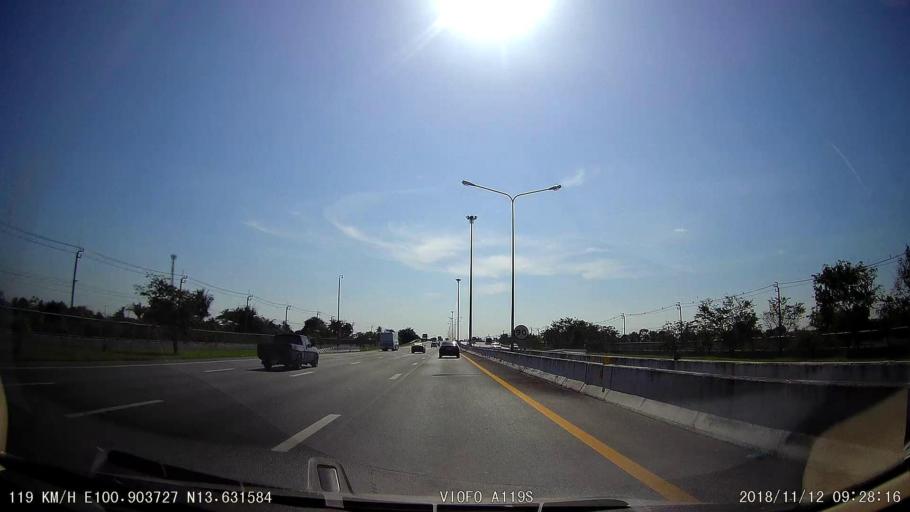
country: TH
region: Samut Prakan
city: Ban Khlong Bang Sao Thong
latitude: 13.6305
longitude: 100.9047
